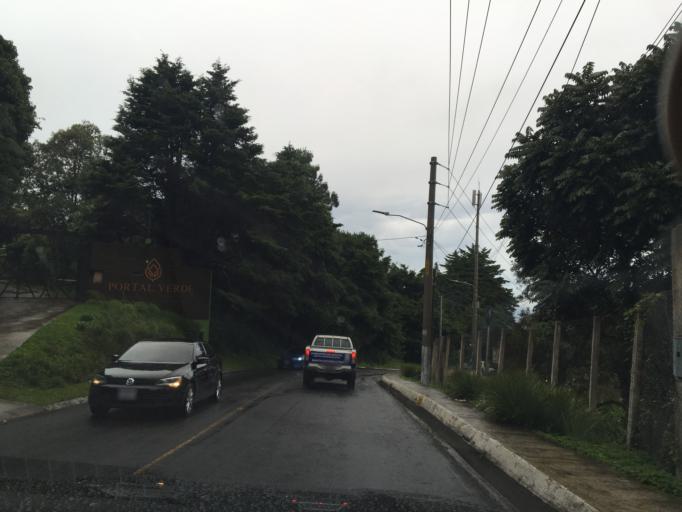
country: GT
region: Guatemala
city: Santa Catarina Pinula
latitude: 14.5537
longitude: -90.4939
